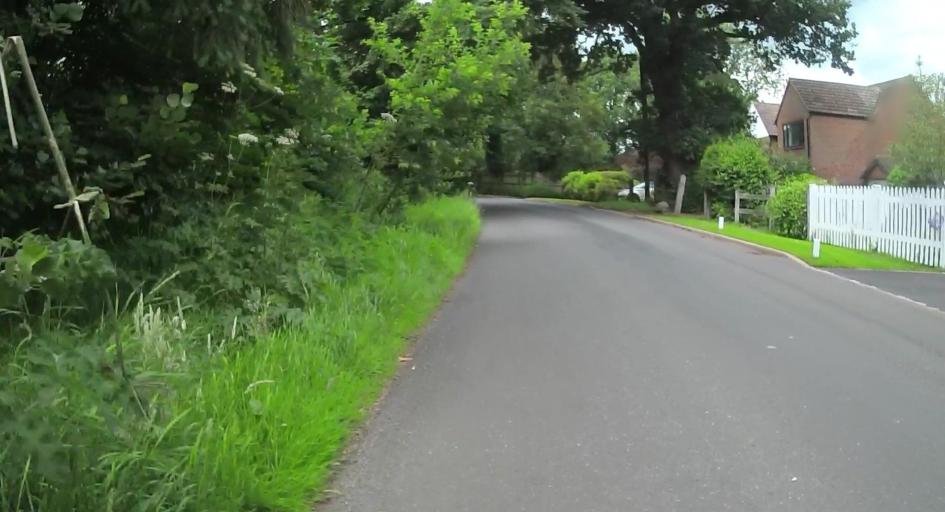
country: GB
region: England
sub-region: Wokingham
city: Wokingham
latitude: 51.3927
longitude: -0.8128
